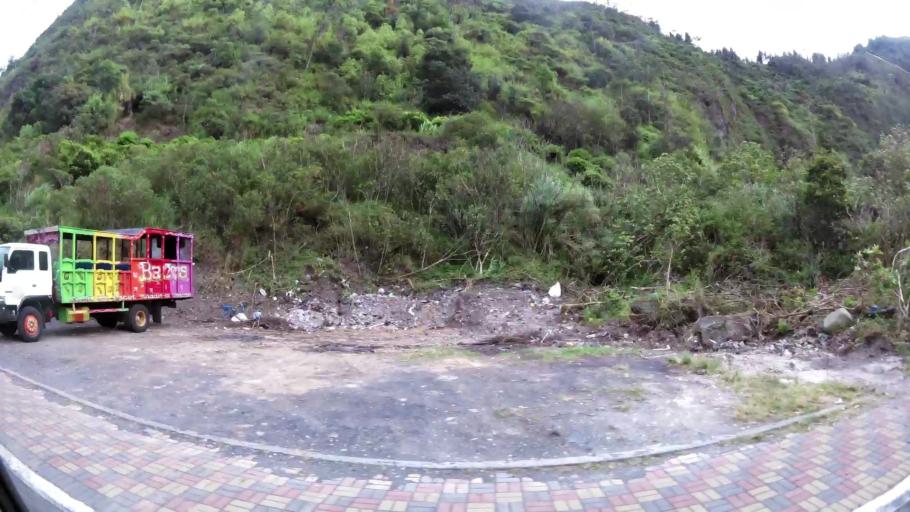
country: EC
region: Tungurahua
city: Banos
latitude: -1.3952
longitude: -78.4031
